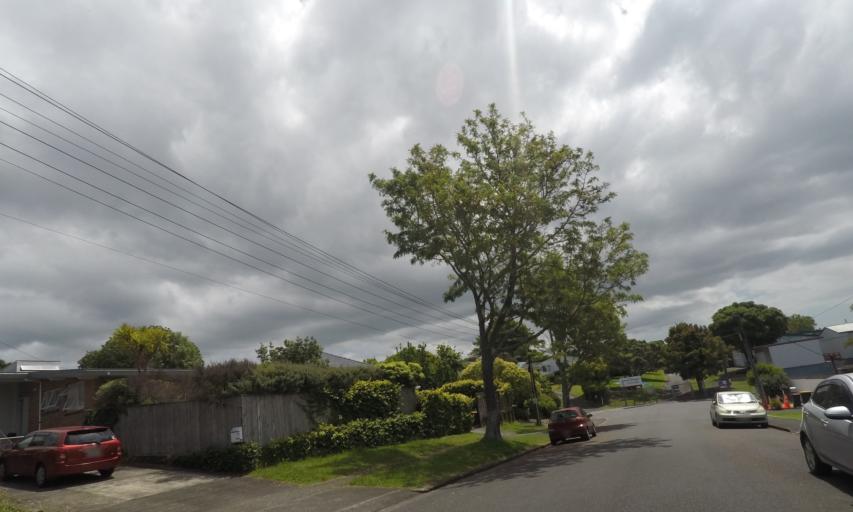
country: NZ
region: Auckland
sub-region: Auckland
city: Waitakere
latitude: -36.9045
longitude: 174.6677
